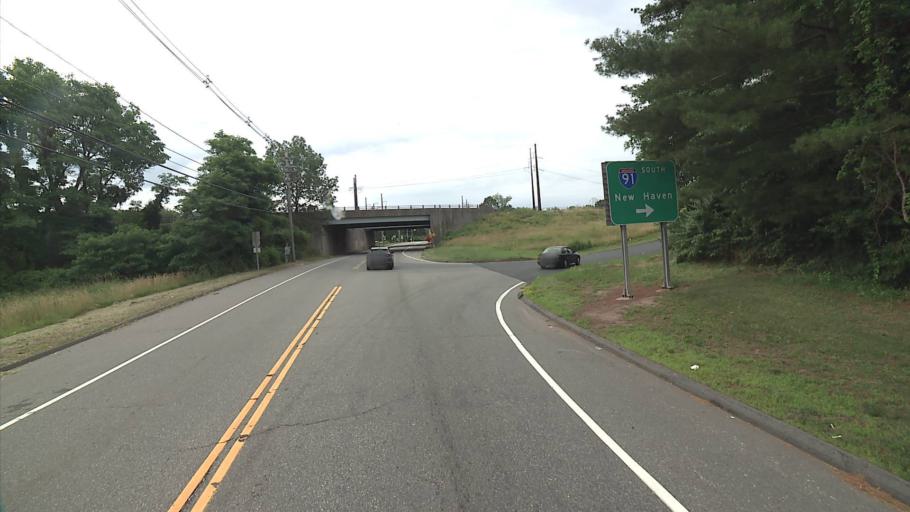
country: US
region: Connecticut
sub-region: New Haven County
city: Wallingford Center
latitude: 41.4349
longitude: -72.8030
